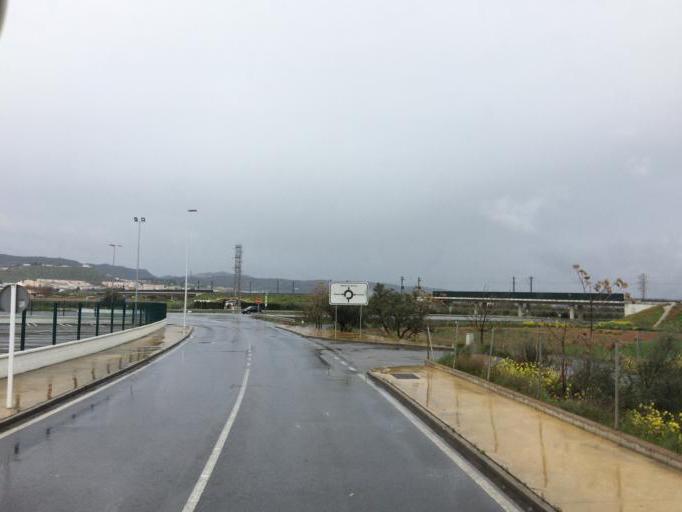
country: ES
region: Andalusia
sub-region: Provincia de Malaga
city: Antequera
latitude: 37.0382
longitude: -4.5317
